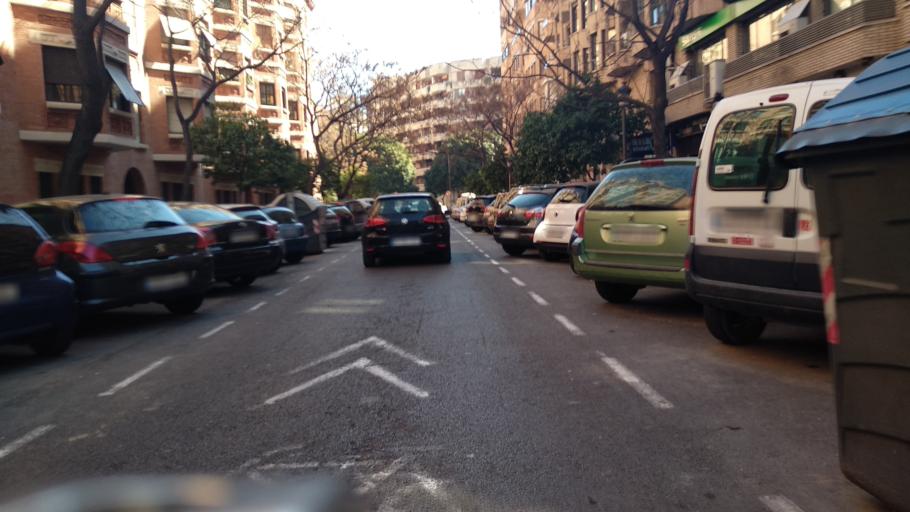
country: ES
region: Valencia
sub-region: Provincia de Valencia
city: Valencia
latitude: 39.4635
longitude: -0.3859
